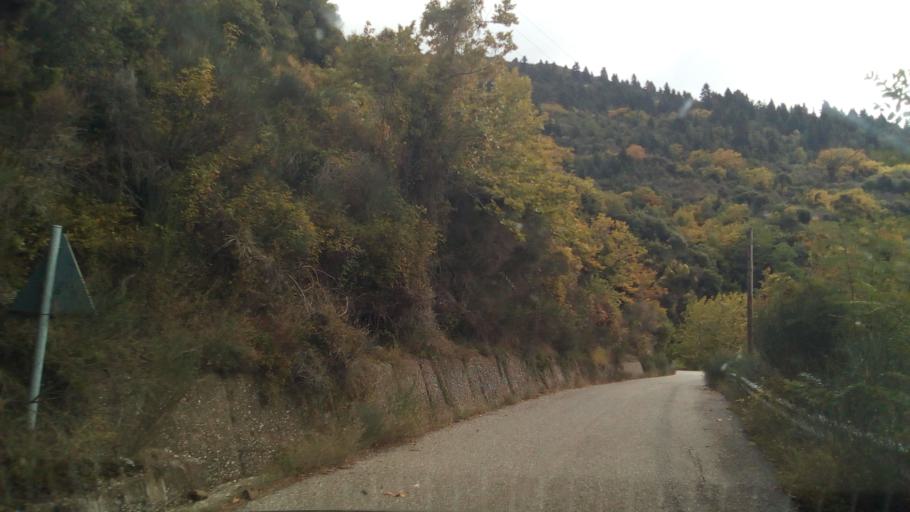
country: GR
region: West Greece
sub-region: Nomos Aitolias kai Akarnanias
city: Nafpaktos
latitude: 38.5389
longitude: 21.8174
